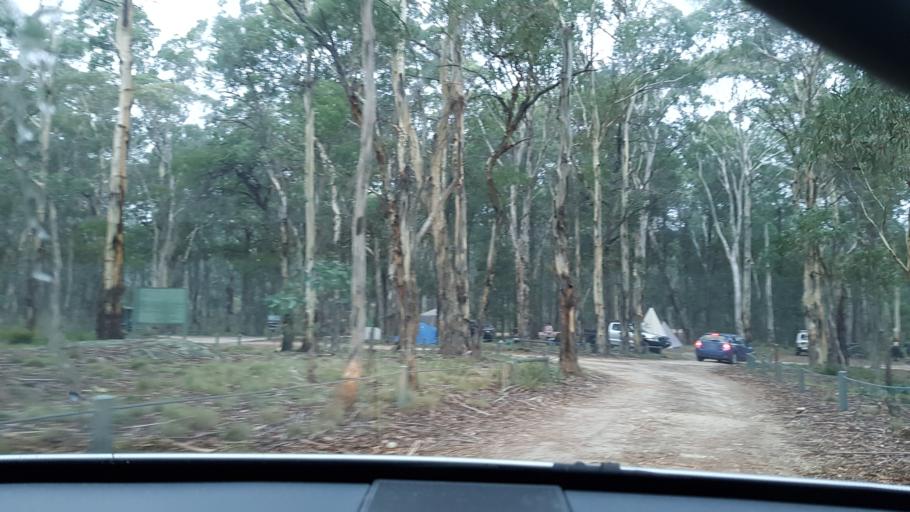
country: AU
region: New South Wales
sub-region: Oberon
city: Oberon
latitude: -33.9712
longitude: 150.0563
